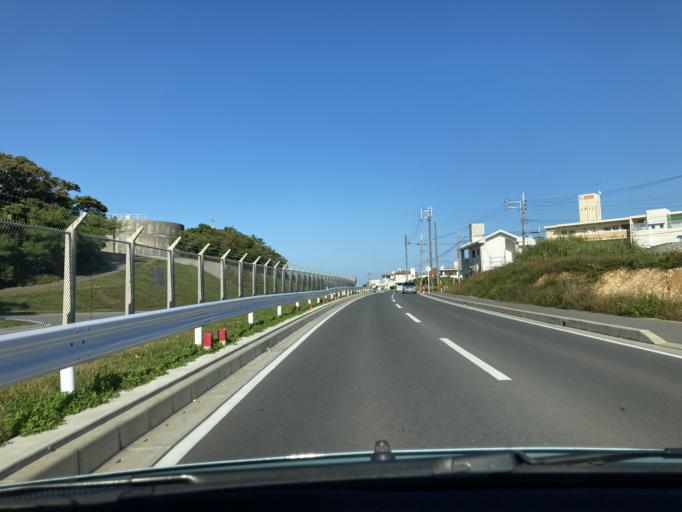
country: JP
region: Okinawa
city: Ginowan
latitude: 26.2695
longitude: 127.7626
